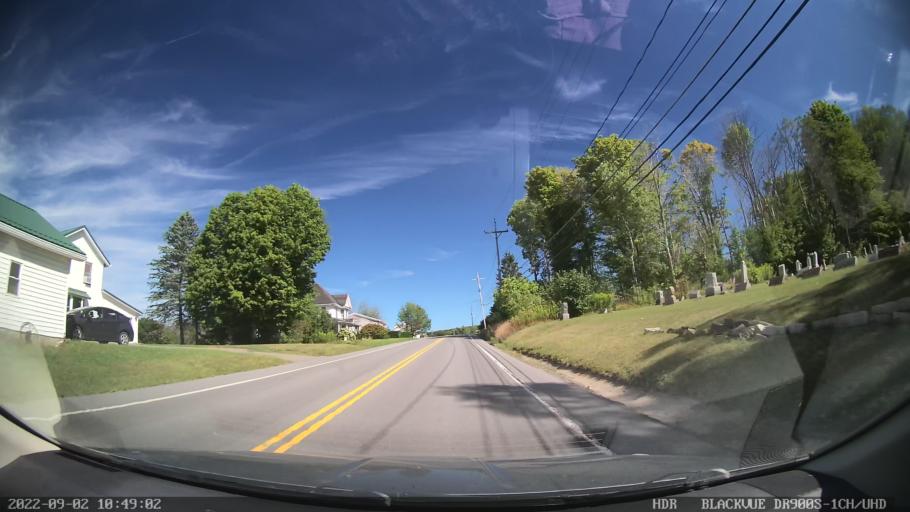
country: US
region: Pennsylvania
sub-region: Tioga County
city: Blossburg
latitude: 41.5949
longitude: -77.1101
